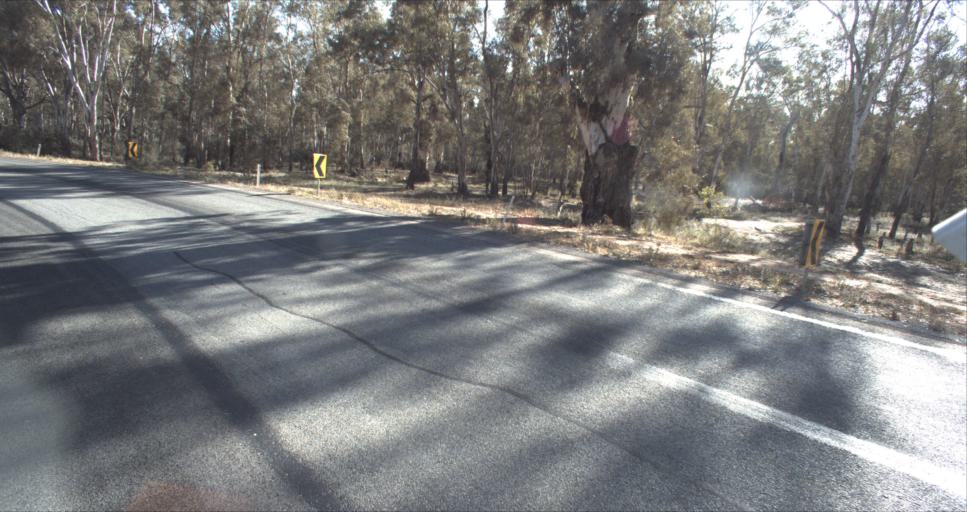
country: AU
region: New South Wales
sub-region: Leeton
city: Leeton
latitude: -34.6317
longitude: 146.3747
